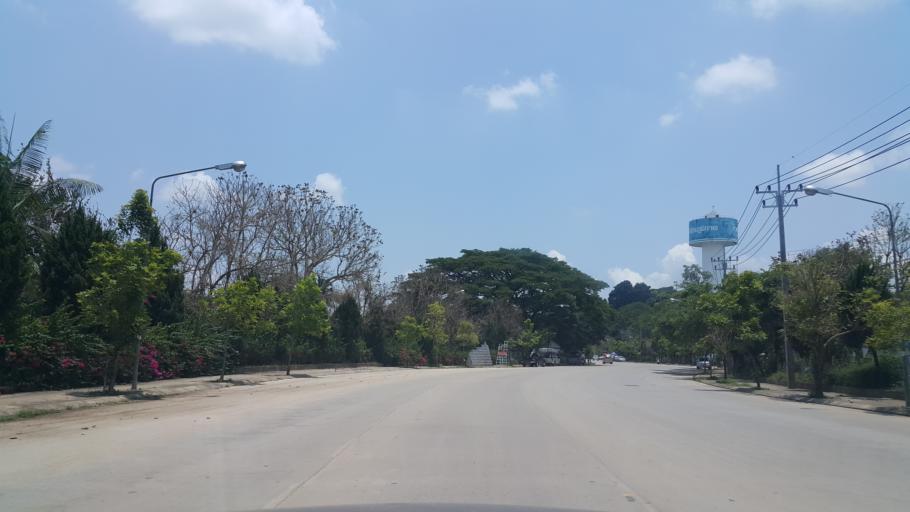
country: TH
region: Chiang Rai
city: Chiang Rai
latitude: 19.9197
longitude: 99.8217
